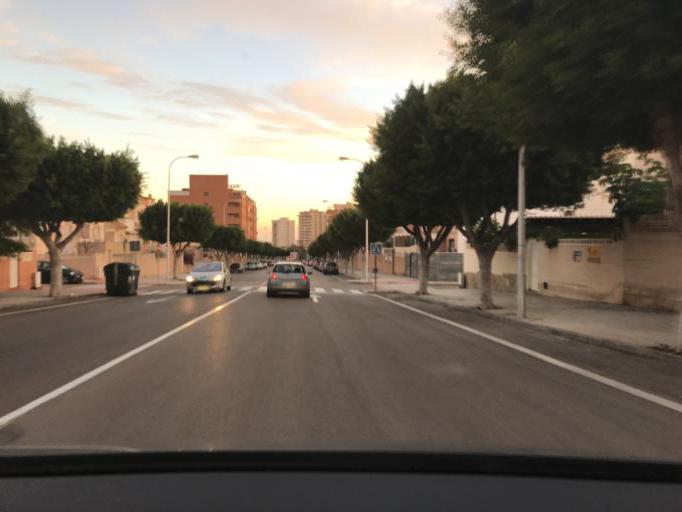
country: ES
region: Andalusia
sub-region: Provincia de Almeria
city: Aguadulce
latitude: 36.8153
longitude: -2.5799
